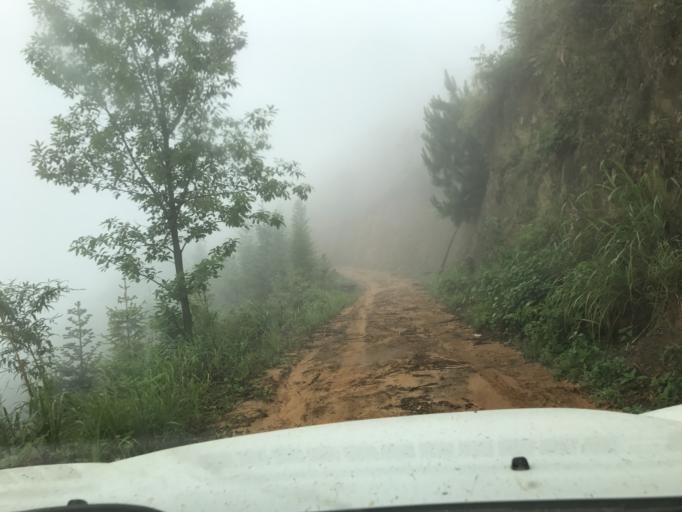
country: CN
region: Guangxi Zhuangzu Zizhiqu
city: Leli
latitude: 24.8070
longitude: 106.0788
